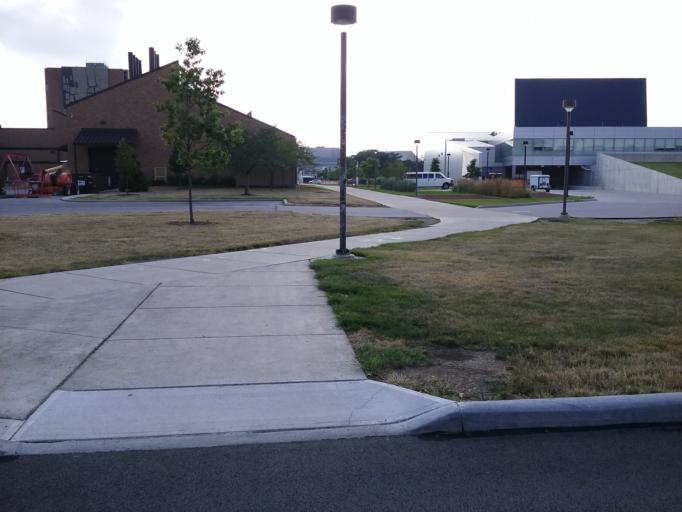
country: US
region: Ohio
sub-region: Wood County
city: Bowling Green
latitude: 41.3770
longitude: -83.6321
